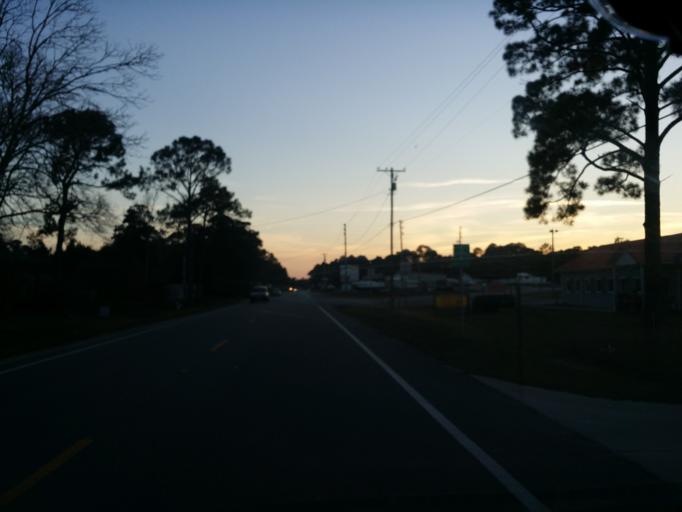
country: US
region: Florida
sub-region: Franklin County
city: Carrabelle
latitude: 29.8428
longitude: -84.6795
